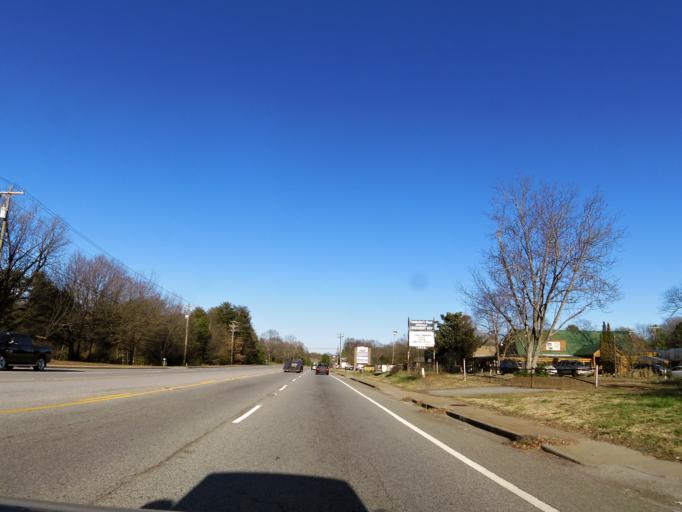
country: US
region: South Carolina
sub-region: Spartanburg County
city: Fairforest
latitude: 34.9091
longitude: -82.0194
